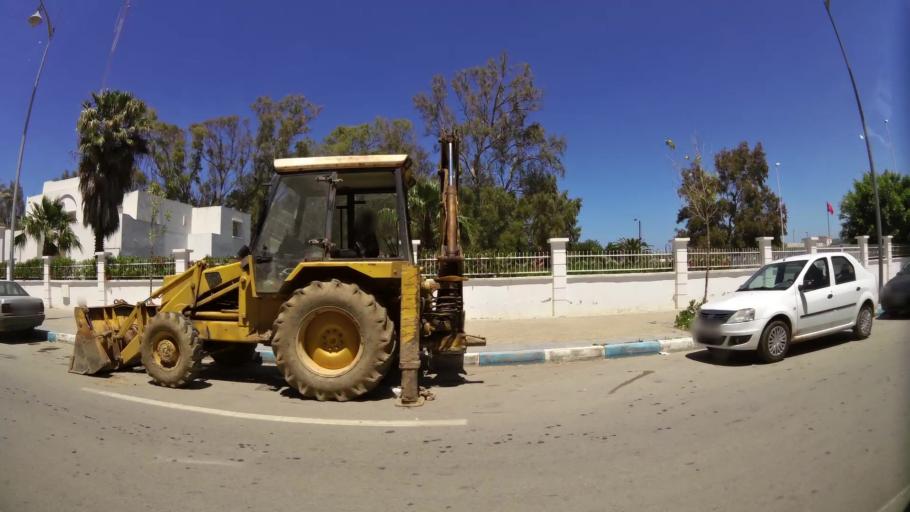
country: MA
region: Oriental
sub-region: Berkane-Taourirt
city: Madagh
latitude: 35.0811
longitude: -2.2169
